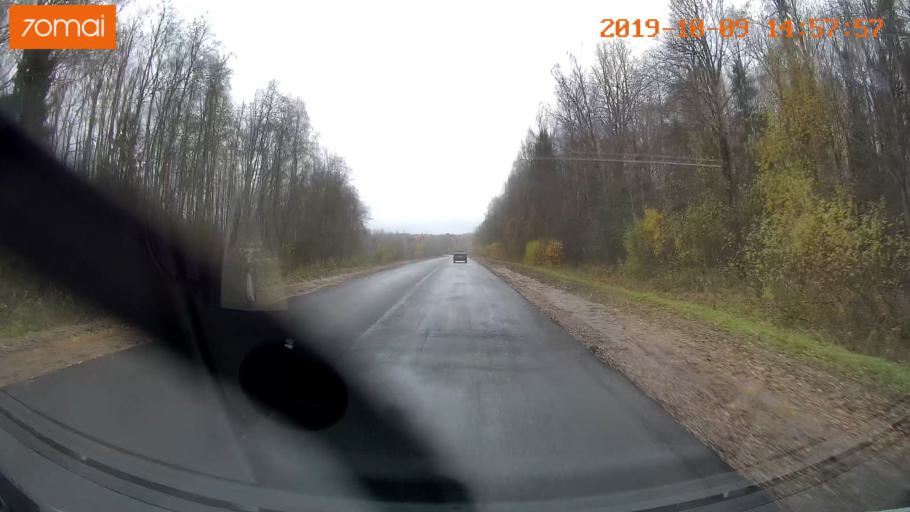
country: RU
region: Kostroma
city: Chistyye Bory
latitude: 58.3320
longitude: 41.6531
